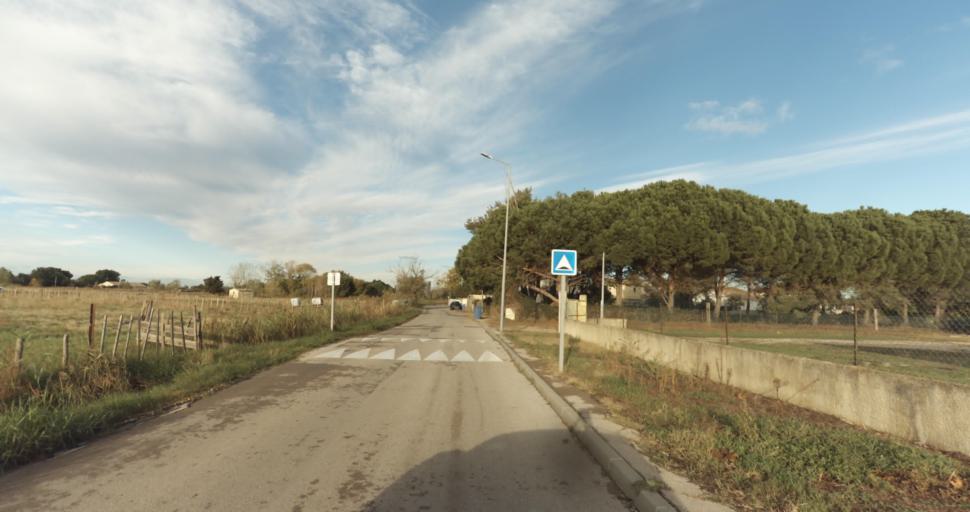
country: FR
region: Languedoc-Roussillon
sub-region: Departement du Gard
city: Aigues-Mortes
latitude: 43.5612
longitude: 4.2048
